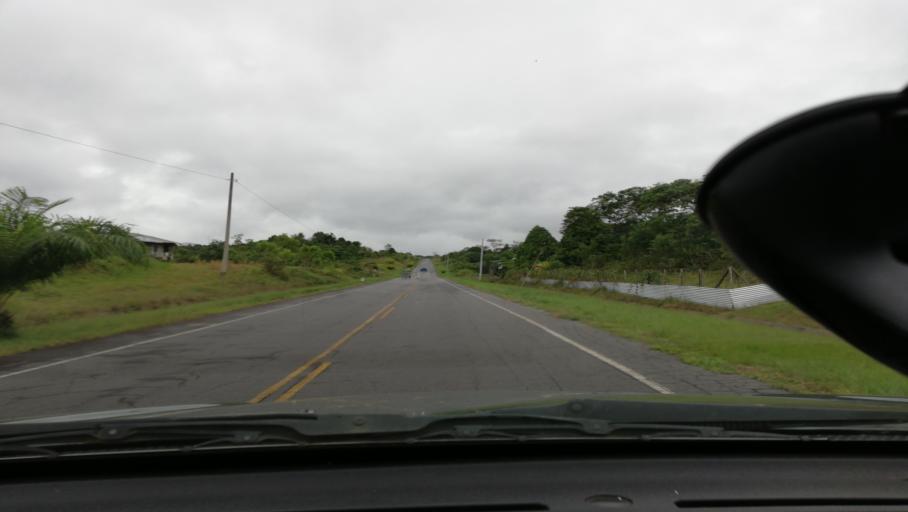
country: PE
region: Loreto
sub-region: Provincia de Loreto
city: Nauta
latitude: -4.3523
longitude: -73.5467
